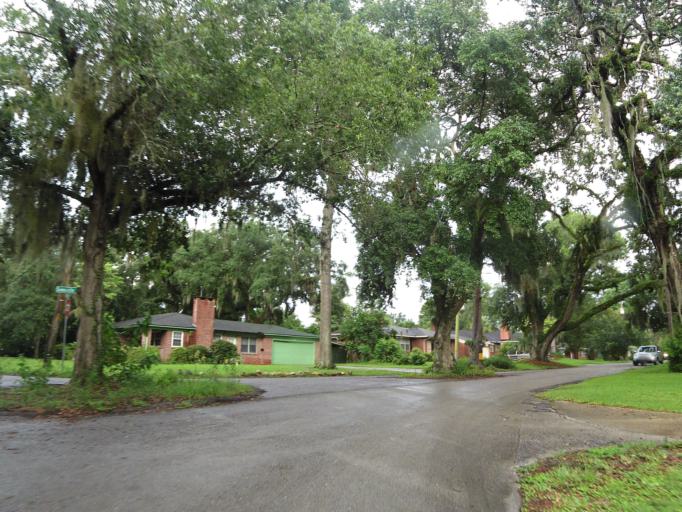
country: US
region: Florida
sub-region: Duval County
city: Jacksonville
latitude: 30.3098
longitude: -81.6265
